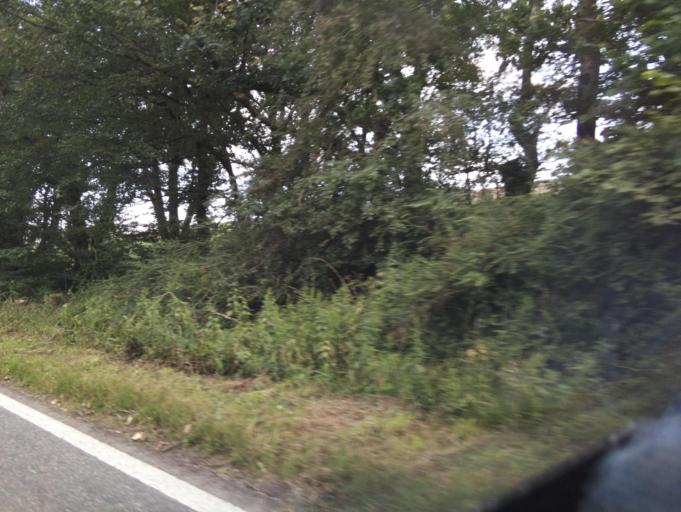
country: GB
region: England
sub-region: Somerset
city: Shepton Mallet
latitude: 51.2062
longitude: -2.4940
